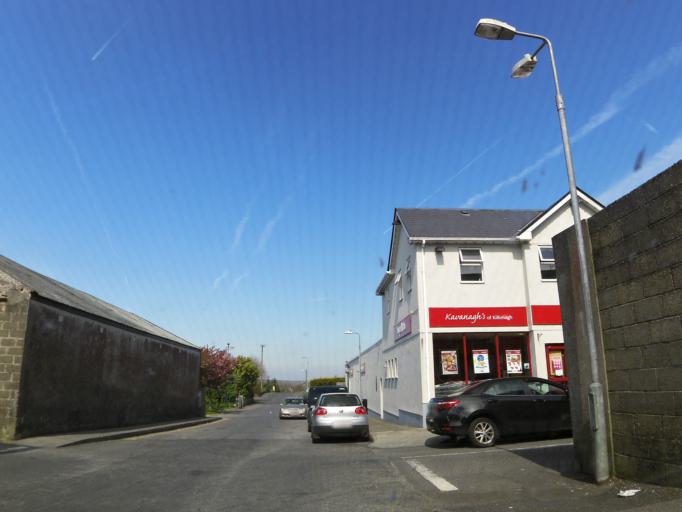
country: IE
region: Connaught
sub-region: Maigh Eo
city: Kiltamagh
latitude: 53.8503
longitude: -8.9991
